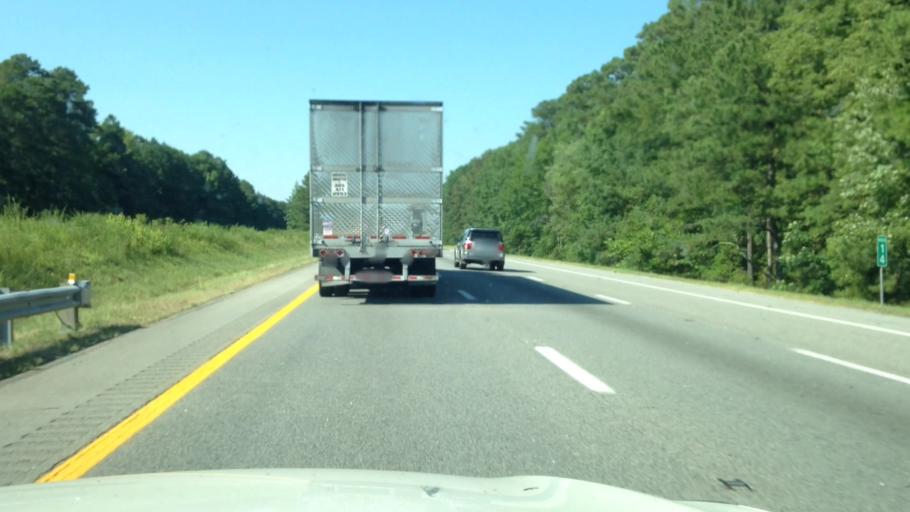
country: US
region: Virginia
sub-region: City of Emporia
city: Emporia
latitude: 36.7369
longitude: -77.5196
